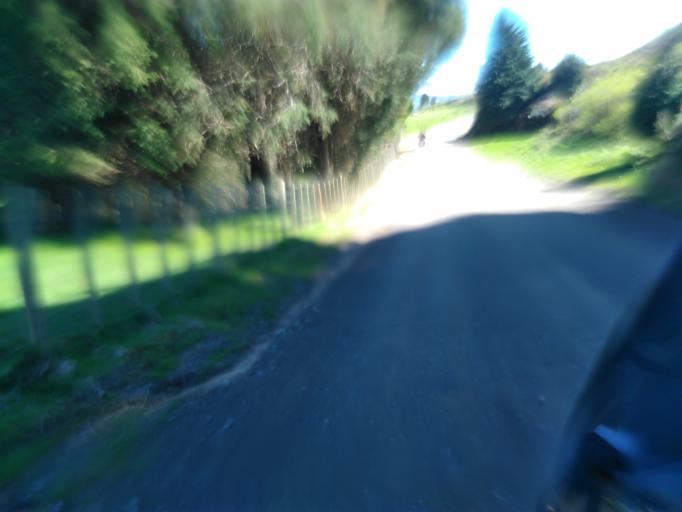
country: NZ
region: Bay of Plenty
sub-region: Opotiki District
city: Opotiki
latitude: -38.3111
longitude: 177.5648
